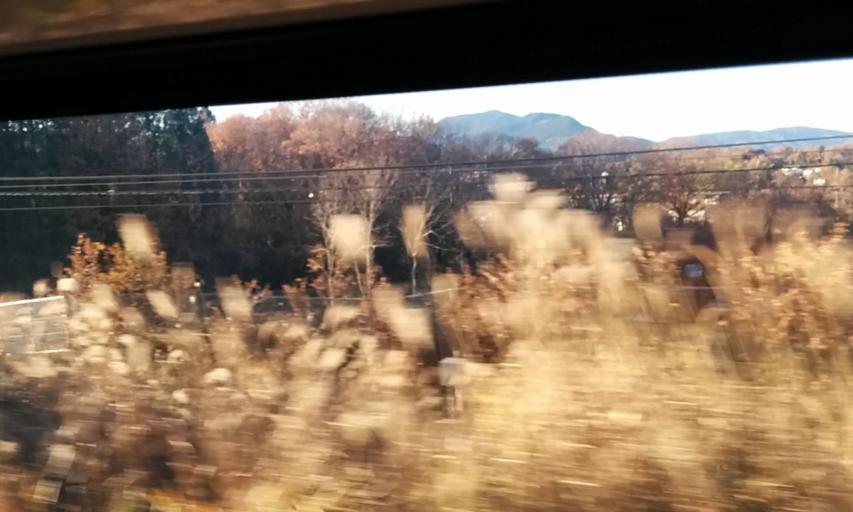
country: JP
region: Gifu
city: Nakatsugawa
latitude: 35.4681
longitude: 137.4166
